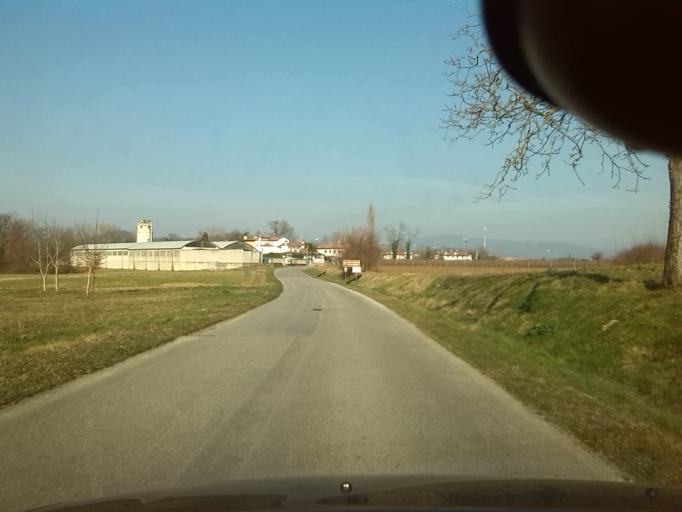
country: IT
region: Friuli Venezia Giulia
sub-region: Provincia di Udine
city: Corno di Rosazzo
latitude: 45.9868
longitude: 13.4325
